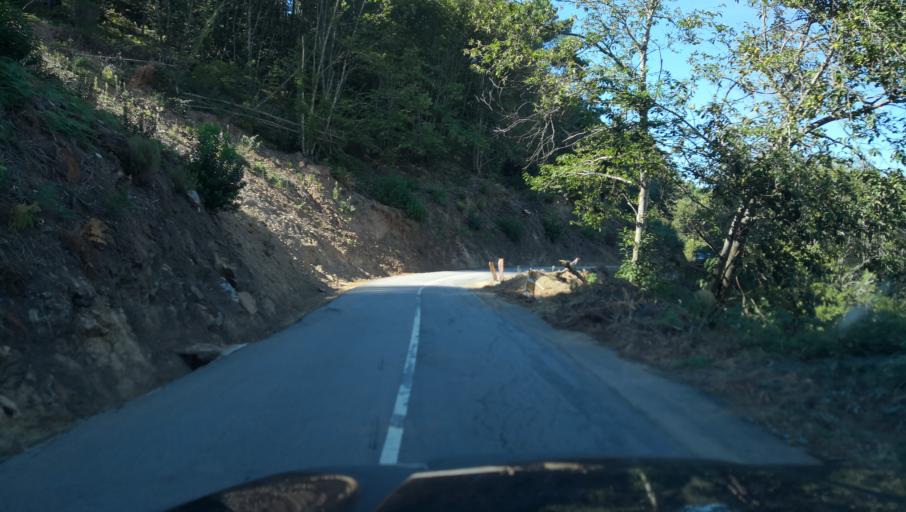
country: PT
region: Vila Real
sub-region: Santa Marta de Penaguiao
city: Santa Marta de Penaguiao
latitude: 41.2370
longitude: -7.7973
